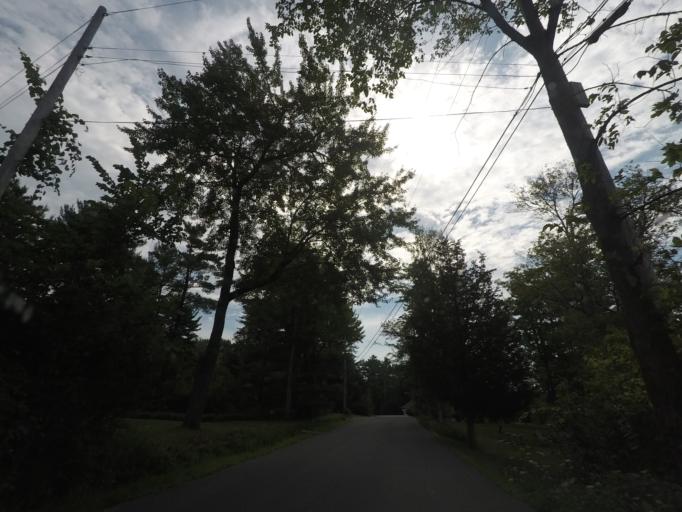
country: US
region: New York
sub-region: Rensselaer County
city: Averill Park
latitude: 42.6419
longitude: -73.5589
